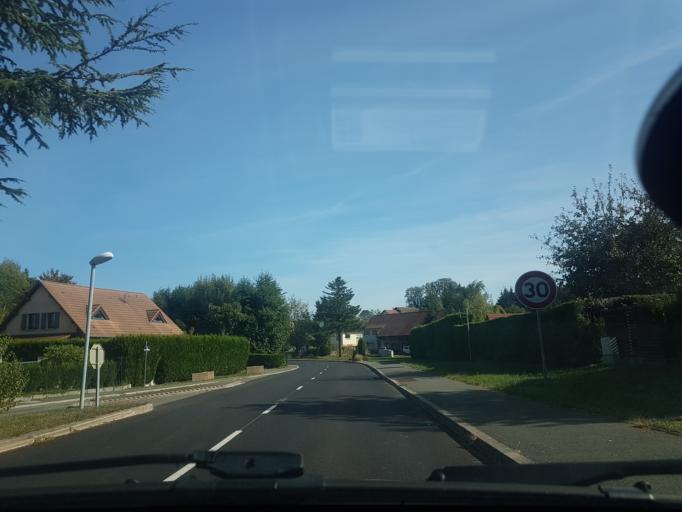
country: FR
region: Franche-Comte
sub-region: Territoire de Belfort
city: Chevremont
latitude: 47.6591
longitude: 6.9134
